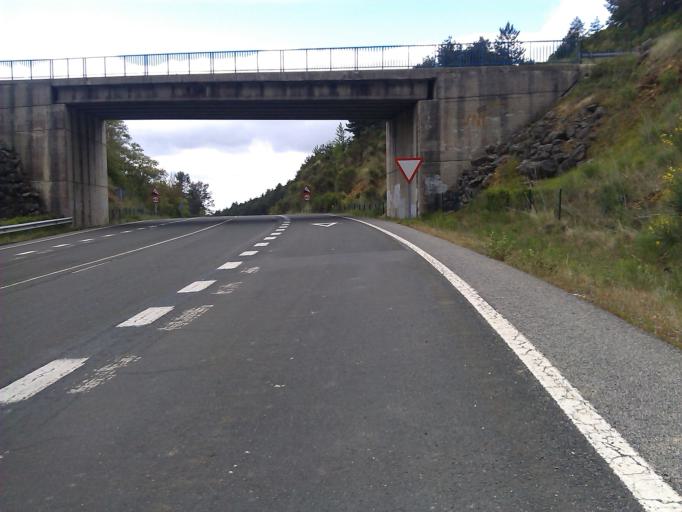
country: ES
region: Navarre
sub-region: Provincia de Navarra
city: Legarda
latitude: 42.7408
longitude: -1.7653
